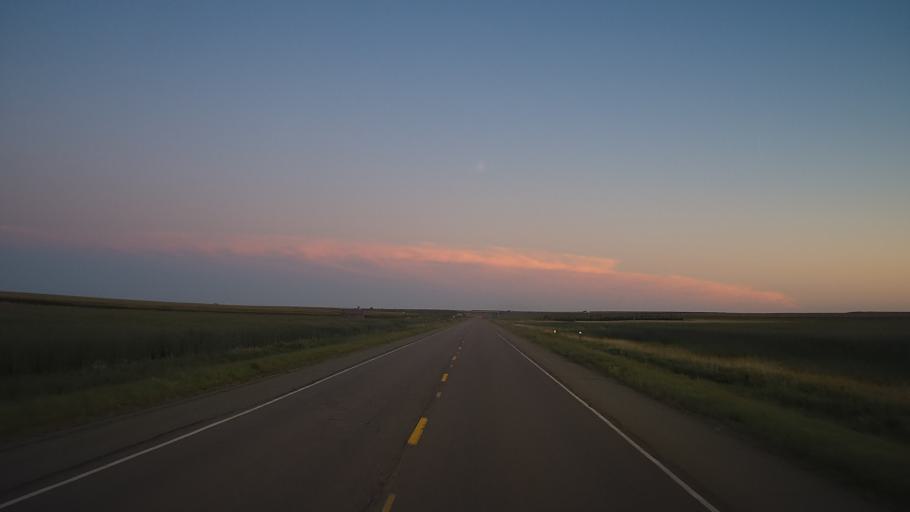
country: US
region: South Dakota
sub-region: Lyman County
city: Kennebec
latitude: 43.8711
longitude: -99.6059
